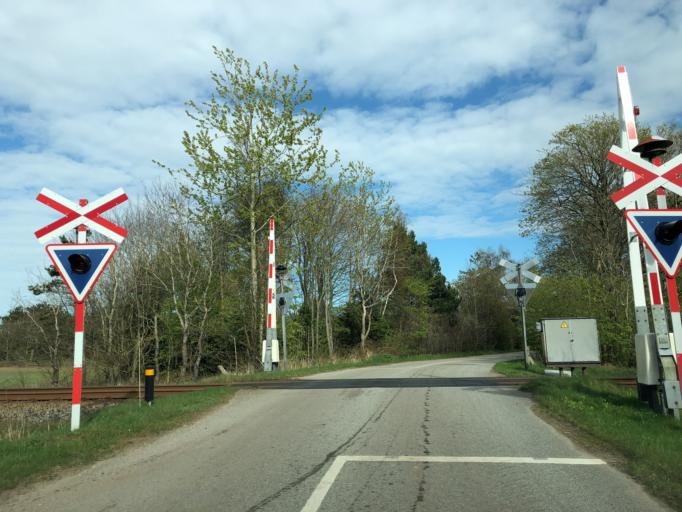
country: DK
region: Central Jutland
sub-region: Holstebro Kommune
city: Ulfborg
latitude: 56.2523
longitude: 8.3220
